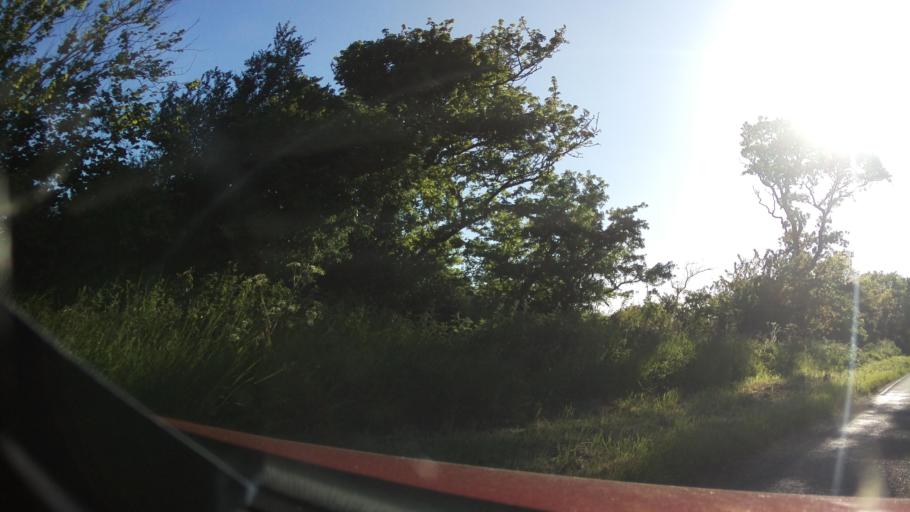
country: GB
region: England
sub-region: Devon
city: Colyton
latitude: 50.7244
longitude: -3.0236
